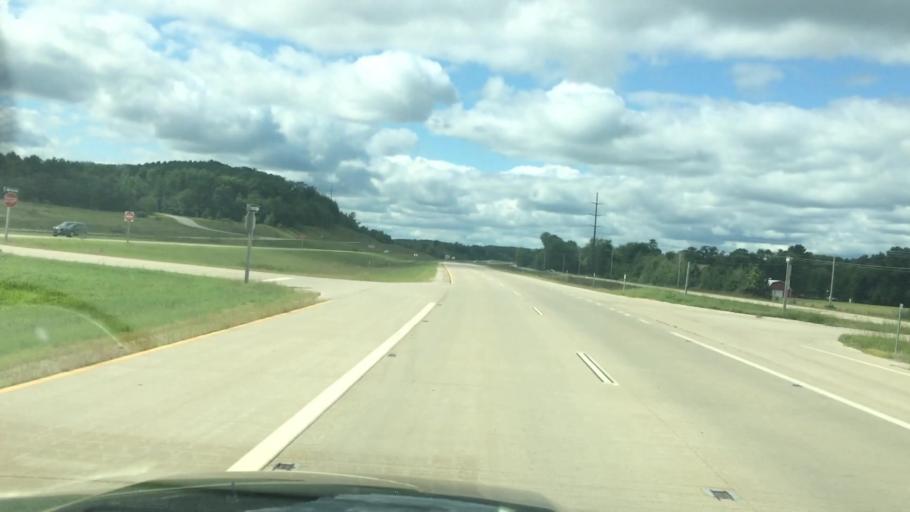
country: US
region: Wisconsin
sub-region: Waupaca County
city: King
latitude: 44.3728
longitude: -89.1531
